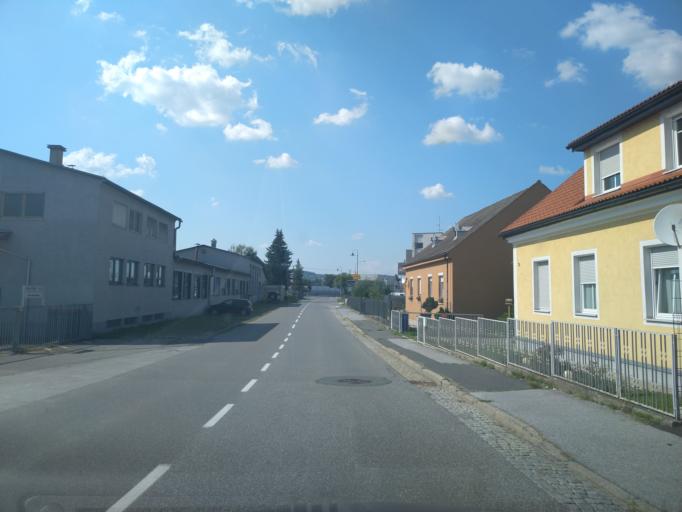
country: AT
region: Styria
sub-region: Politischer Bezirk Leibnitz
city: Leibnitz
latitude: 46.7741
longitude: 15.5509
